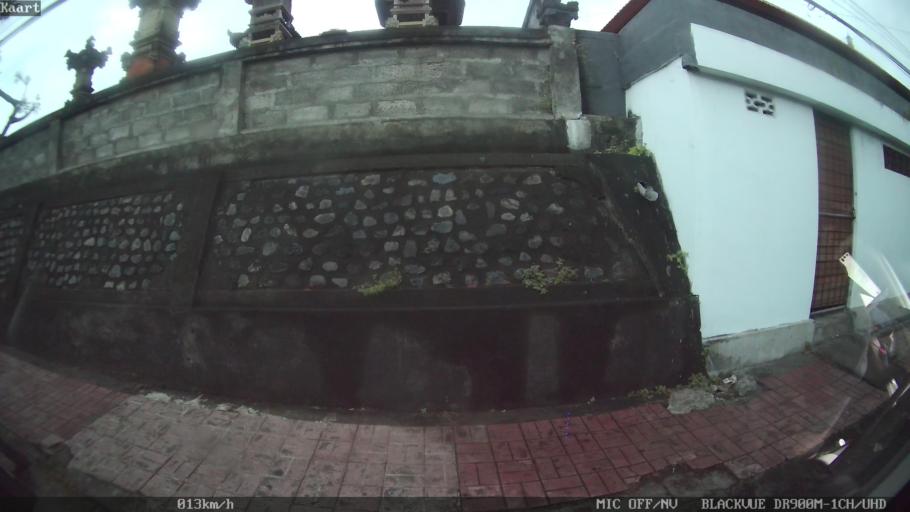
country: ID
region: Bali
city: Banjar Pasekan
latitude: -8.6033
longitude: 115.2809
